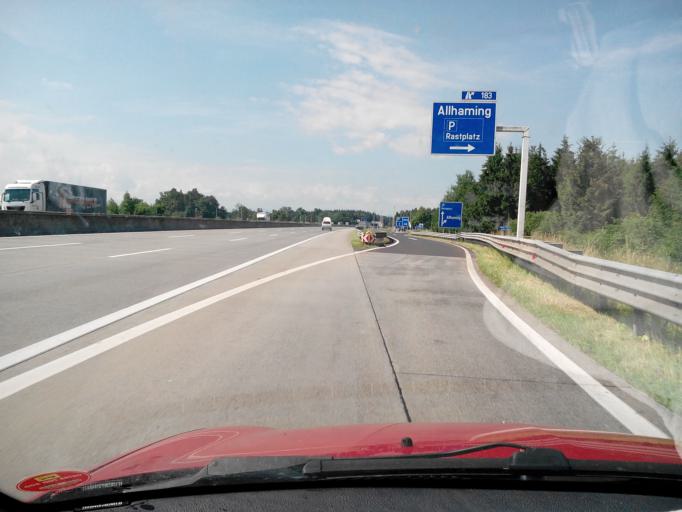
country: AT
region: Upper Austria
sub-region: Wels-Land
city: Marchtrenk
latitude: 48.1589
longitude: 14.1614
